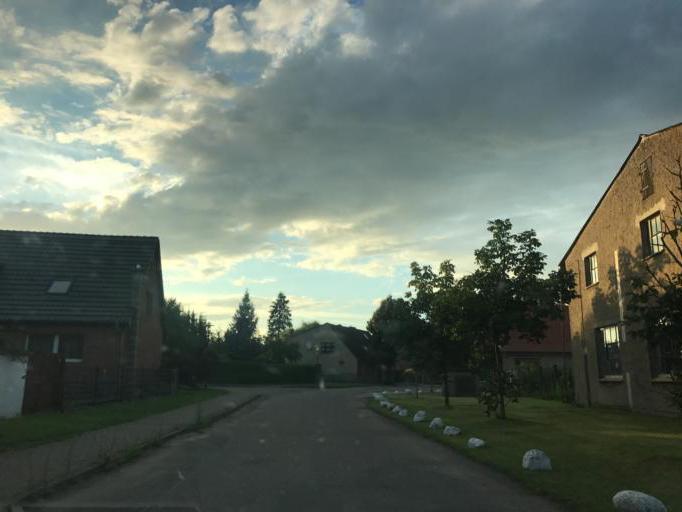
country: DE
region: Mecklenburg-Vorpommern
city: Wesenberg
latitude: 53.2965
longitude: 12.8831
